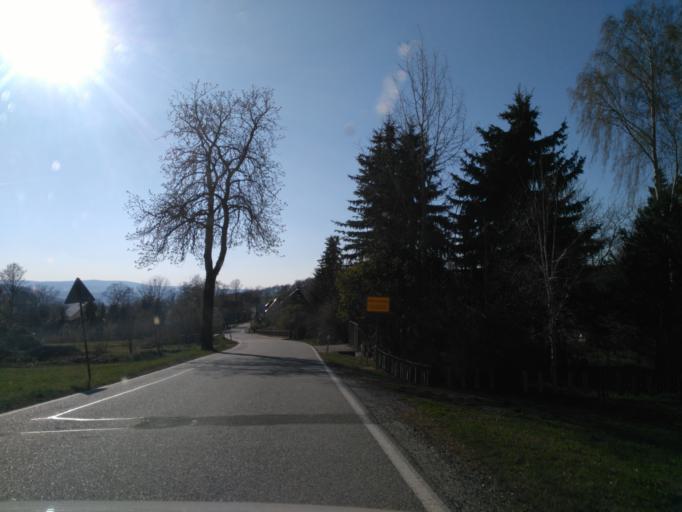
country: DE
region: Saxony
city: Scheibenberg
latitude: 50.5361
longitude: 12.9050
